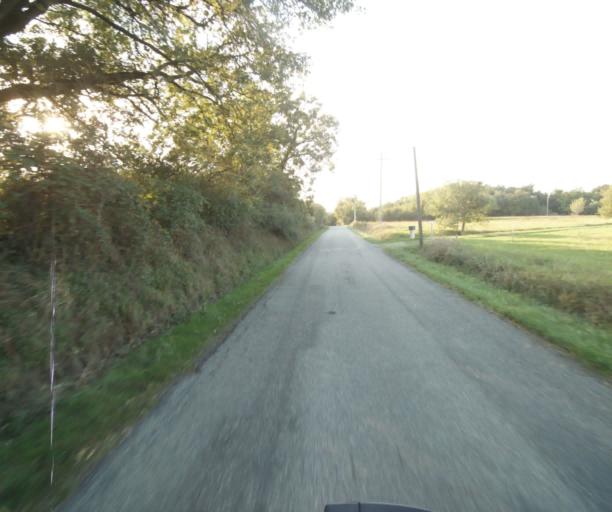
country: FR
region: Midi-Pyrenees
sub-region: Departement du Tarn-et-Garonne
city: Verdun-sur-Garonne
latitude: 43.8358
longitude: 1.1554
